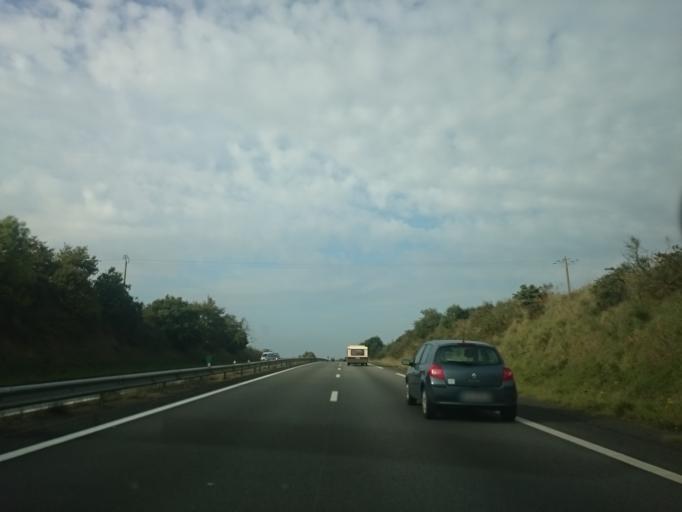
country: FR
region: Brittany
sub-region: Departement des Cotes-d'Armor
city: Broons
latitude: 48.3035
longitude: -2.2344
